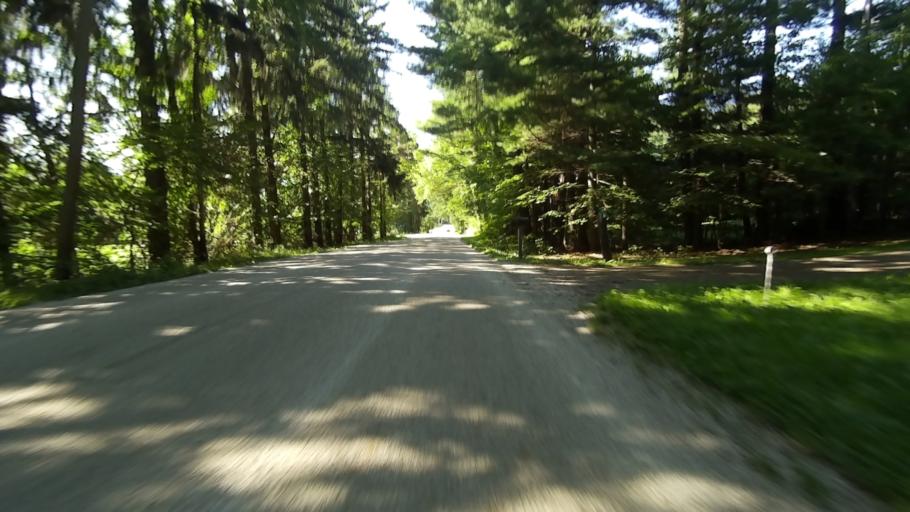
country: US
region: Ohio
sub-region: Portage County
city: Mantua
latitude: 41.2674
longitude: -81.2771
